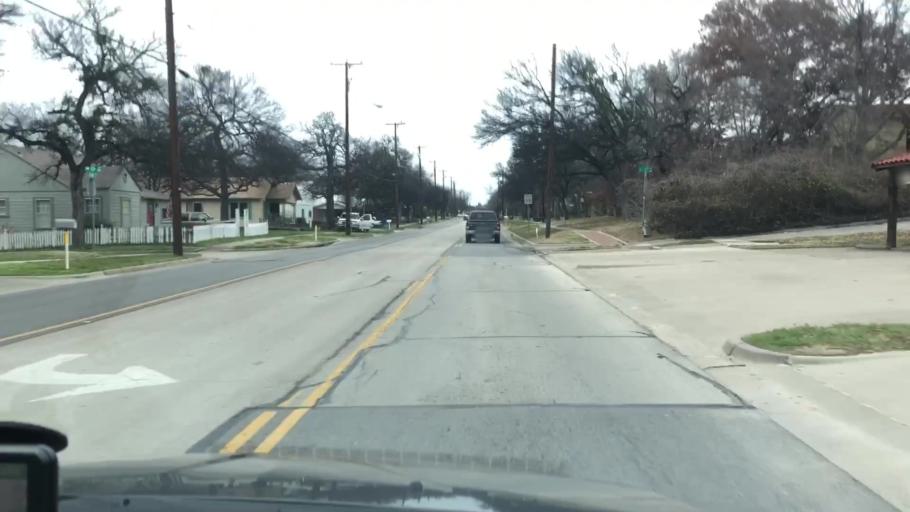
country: US
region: Texas
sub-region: Palo Pinto County
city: Mineral Wells
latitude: 32.8186
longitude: -98.1128
